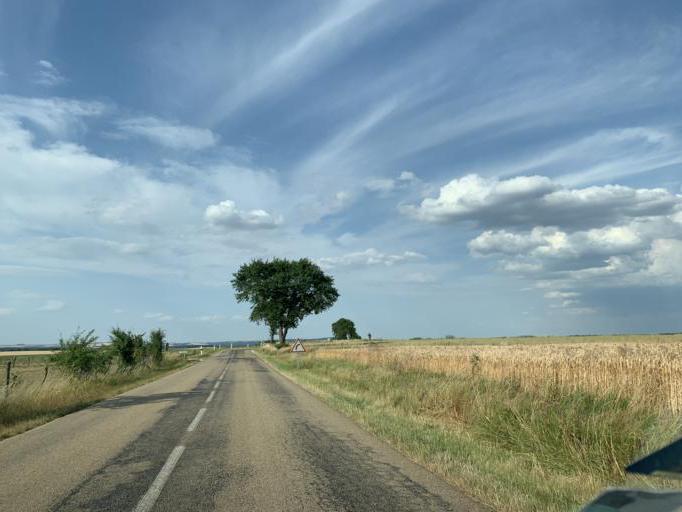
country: FR
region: Bourgogne
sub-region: Departement de l'Yonne
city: Fontenailles
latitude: 47.5054
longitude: 3.3510
